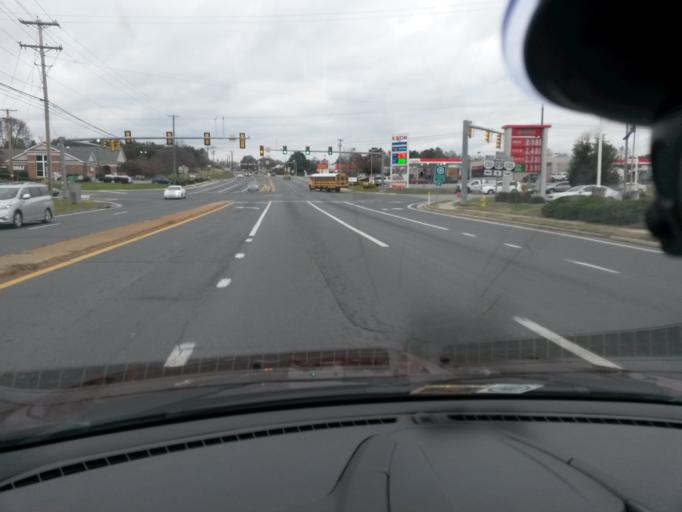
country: US
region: Virginia
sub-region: Amherst County
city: Madison Heights
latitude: 37.4658
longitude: -79.1189
